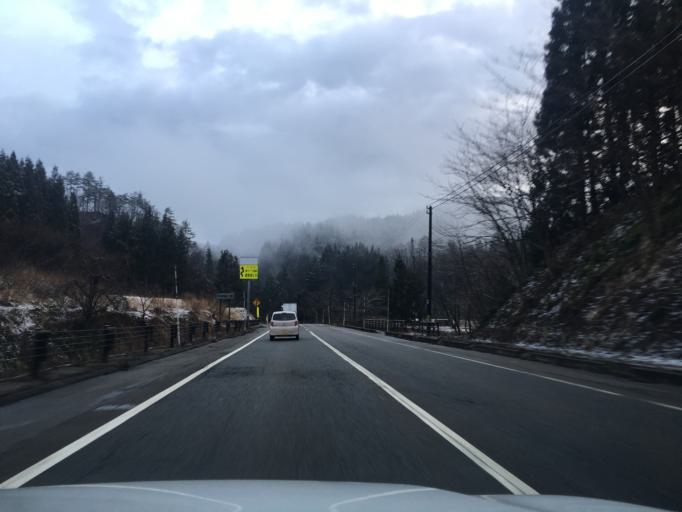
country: JP
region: Niigata
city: Murakami
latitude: 38.4145
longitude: 139.5671
